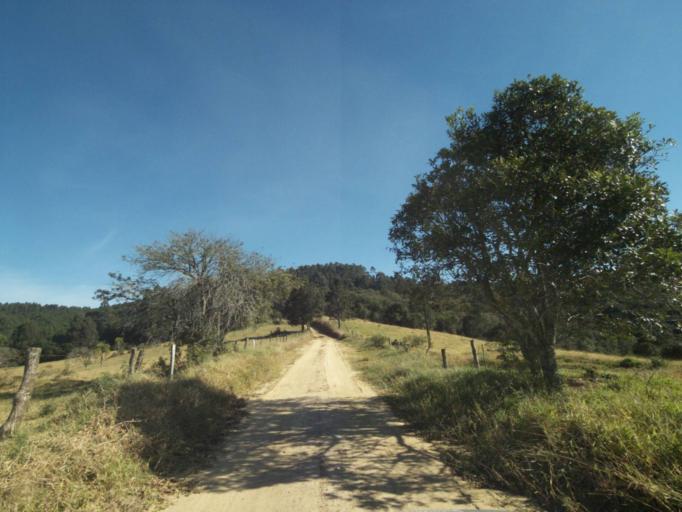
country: BR
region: Parana
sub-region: Tibagi
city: Tibagi
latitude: -24.5508
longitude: -50.4713
